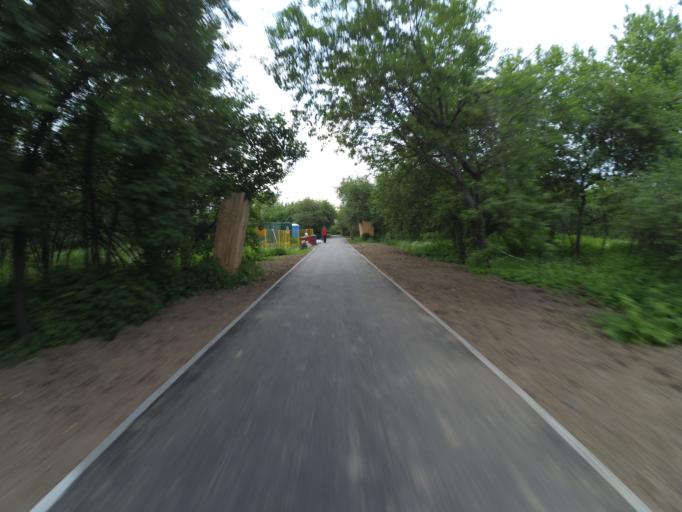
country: RU
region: Moscow
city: Kolomenskoye
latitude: 55.6576
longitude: 37.6603
